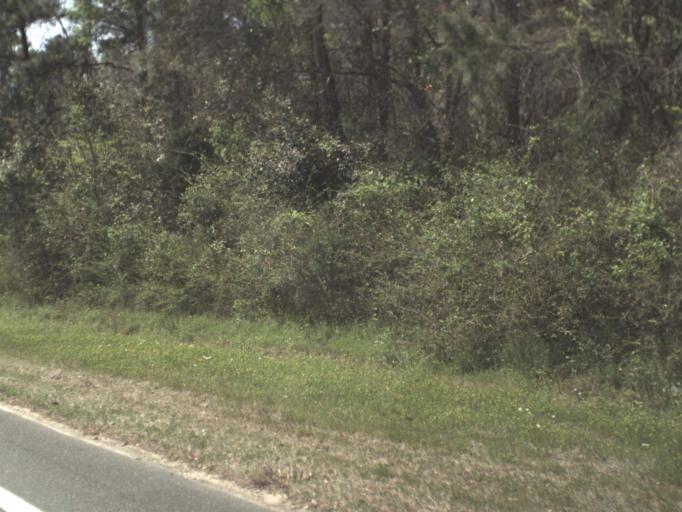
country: US
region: Florida
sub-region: Gadsden County
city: Havana
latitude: 30.6451
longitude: -84.4170
